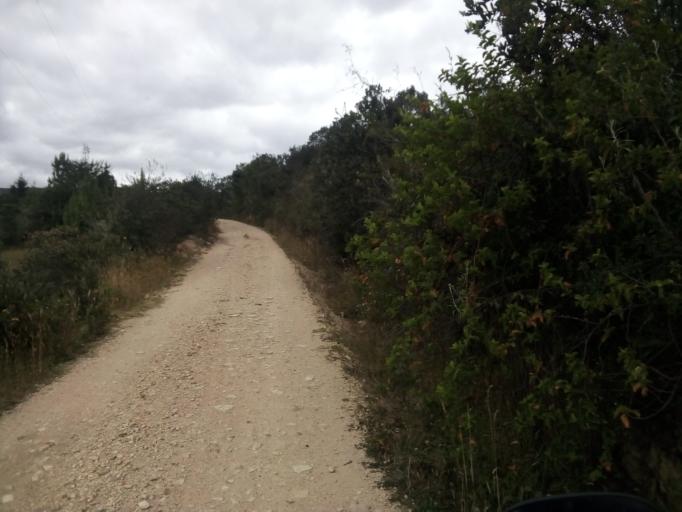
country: CO
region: Boyaca
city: Toca
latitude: 5.5904
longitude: -73.1307
